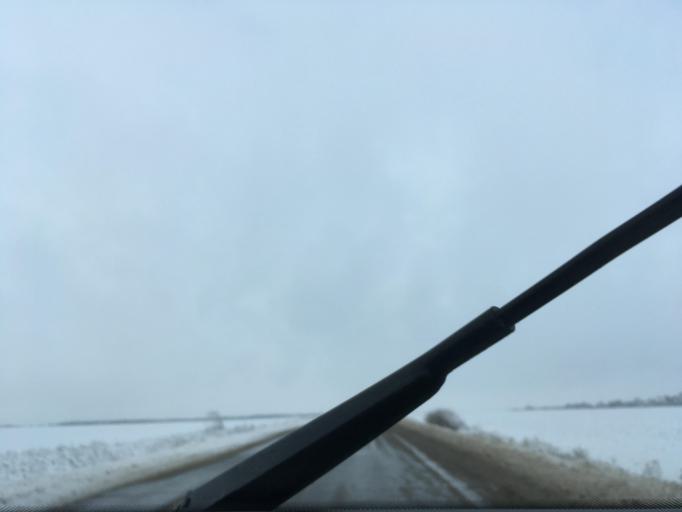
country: RU
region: Voronezj
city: Ol'khovatka
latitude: 50.1387
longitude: 39.2048
